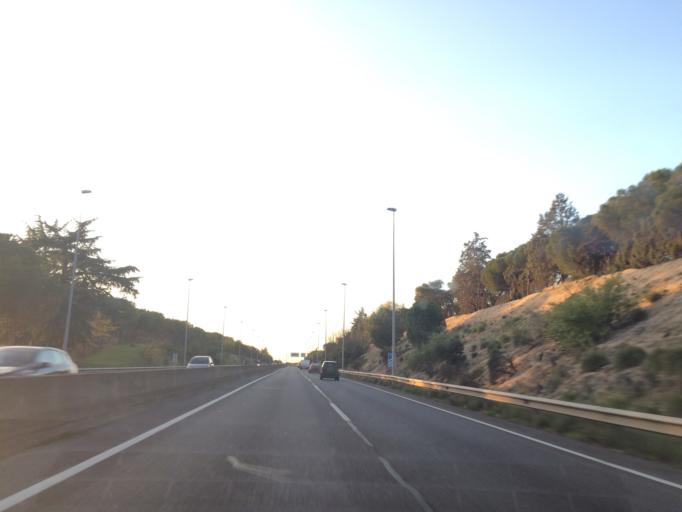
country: ES
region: Madrid
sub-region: Provincia de Madrid
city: Moncloa-Aravaca
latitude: 40.4457
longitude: -3.7547
